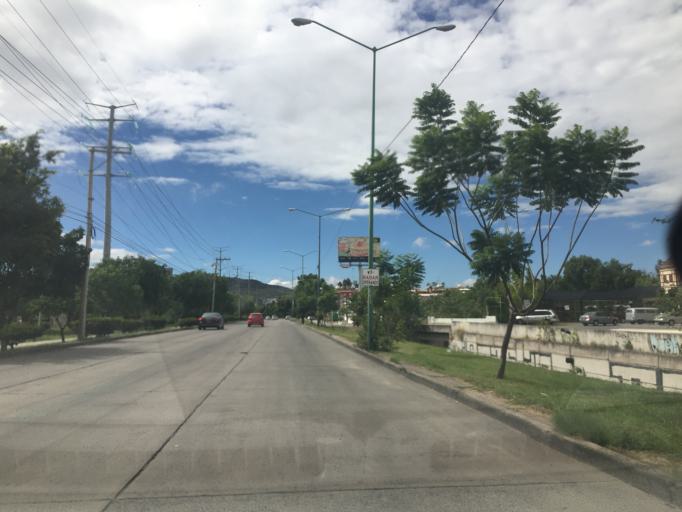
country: MX
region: Guanajuato
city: Leon
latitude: 21.1536
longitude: -101.6787
